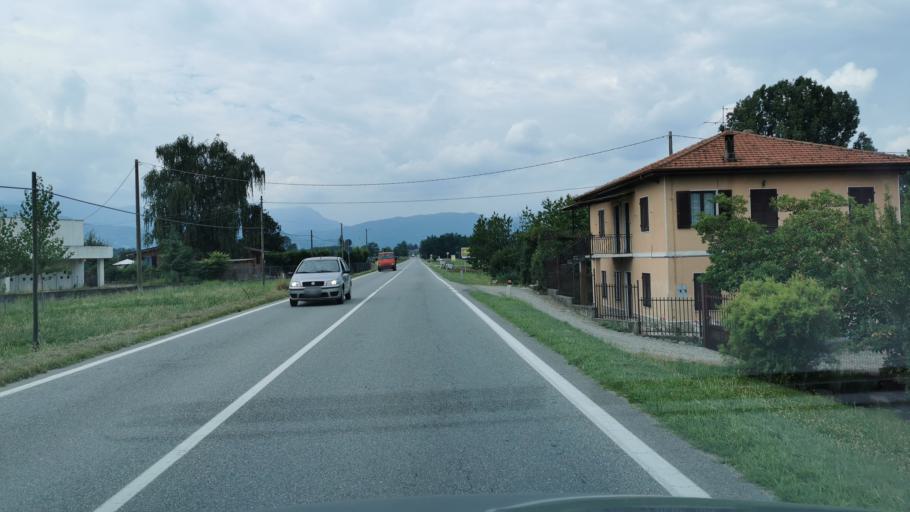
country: IT
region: Piedmont
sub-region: Provincia di Torino
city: Garzigliana
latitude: 44.8317
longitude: 7.3655
